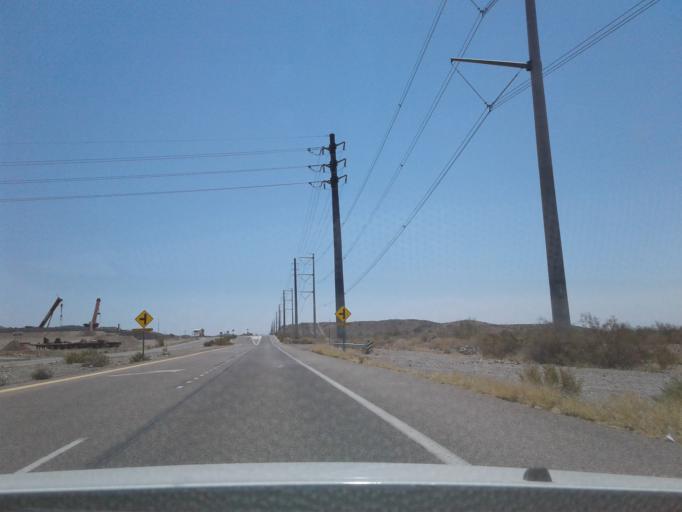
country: US
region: Arizona
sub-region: Maricopa County
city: Laveen
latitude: 33.2908
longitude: -112.1004
